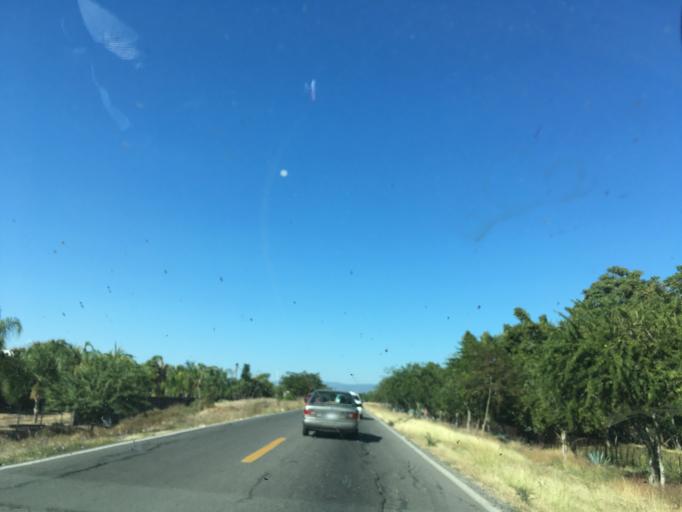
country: MX
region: Michoacan
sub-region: Gabriel Zamora
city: Lombardia
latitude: 19.0915
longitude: -102.0584
